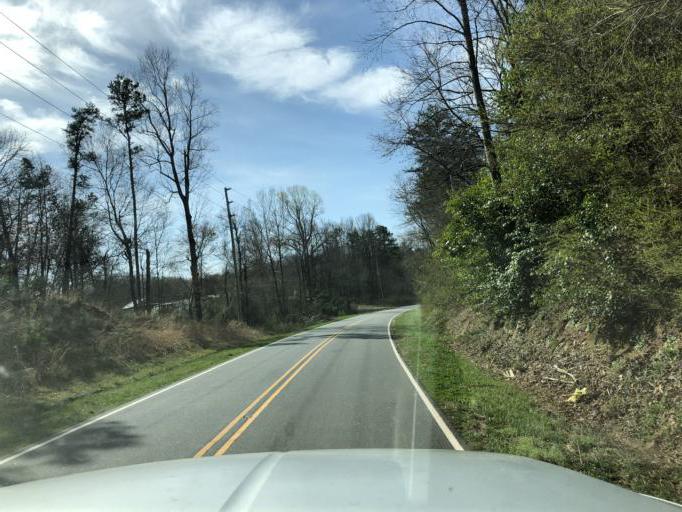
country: US
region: North Carolina
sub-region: Cleveland County
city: Shelby
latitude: 35.4340
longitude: -81.6409
